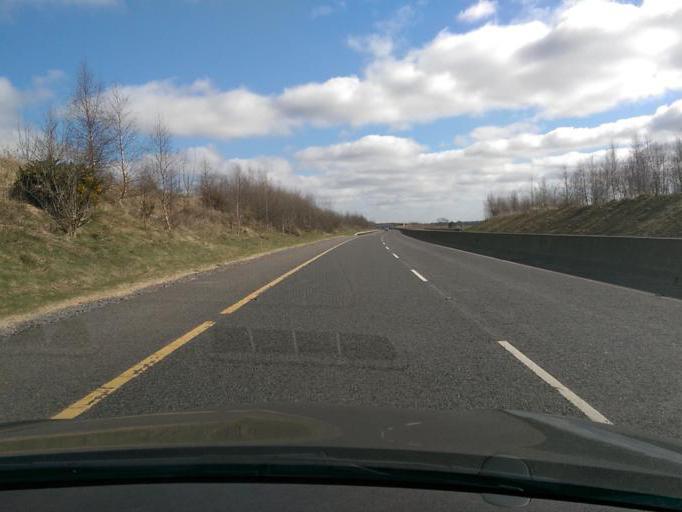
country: IE
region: Leinster
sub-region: An Iarmhi
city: Rathwire
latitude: 53.4484
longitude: -7.1845
